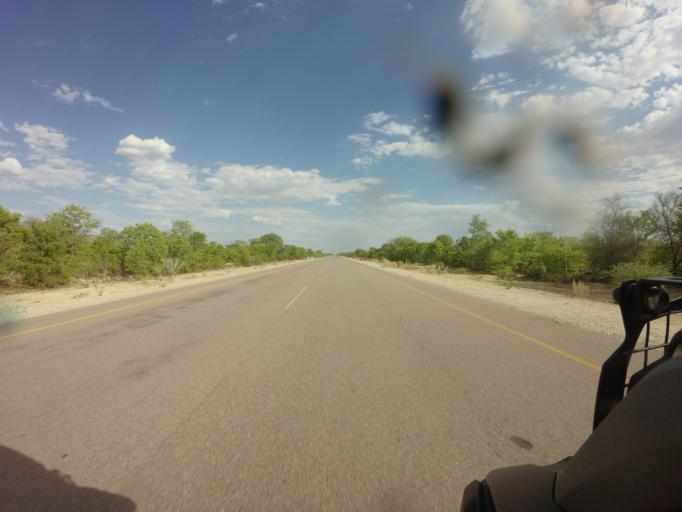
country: AO
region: Cunene
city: Ondjiva
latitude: -16.7765
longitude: 15.4039
